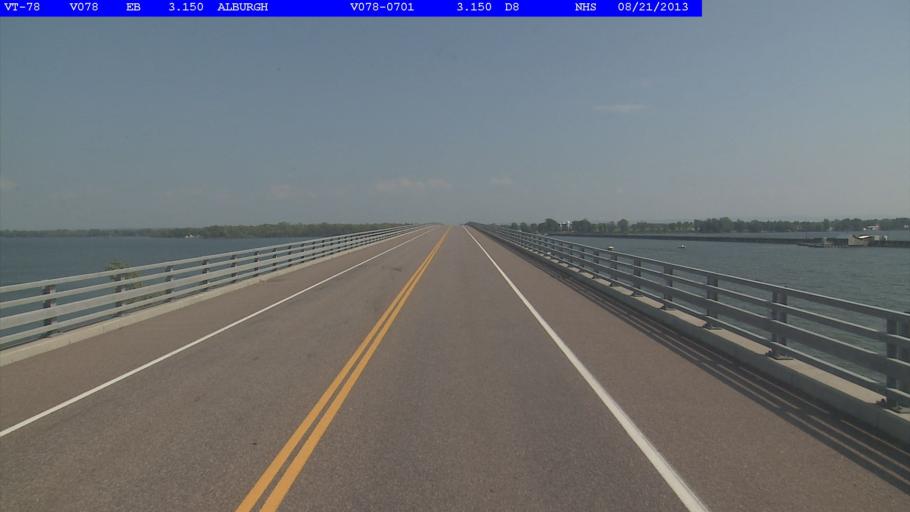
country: US
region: Vermont
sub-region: Franklin County
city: Swanton
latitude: 44.9740
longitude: -73.2238
